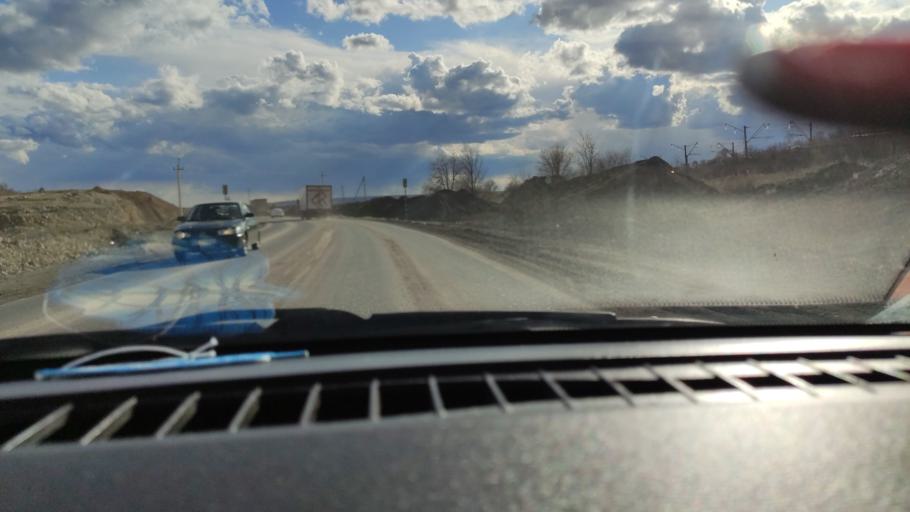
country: RU
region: Saratov
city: Sinodskoye
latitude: 52.0074
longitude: 46.6849
